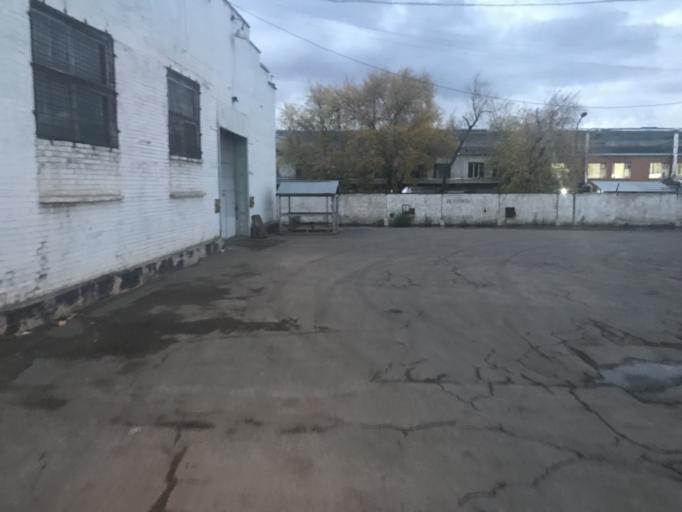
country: KZ
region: Astana Qalasy
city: Astana
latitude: 51.1830
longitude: 71.4301
